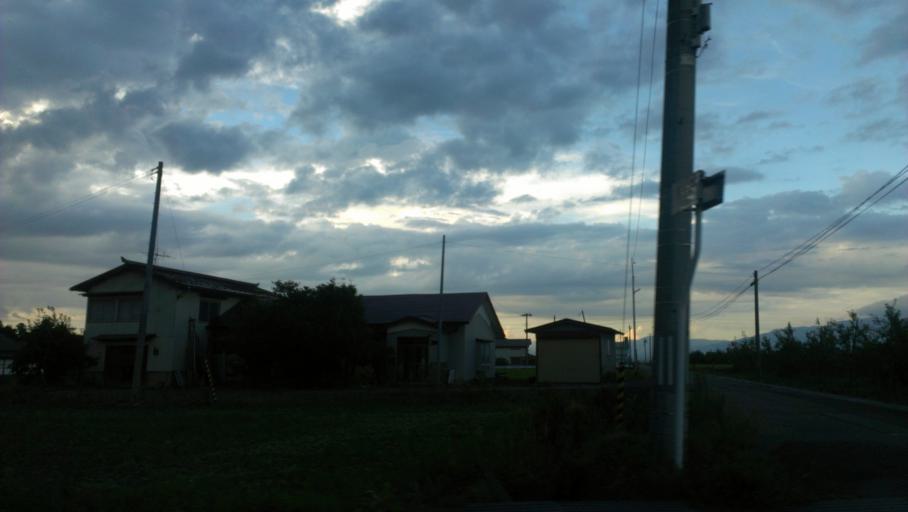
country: JP
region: Fukushima
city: Kitakata
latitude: 37.4571
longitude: 139.8829
